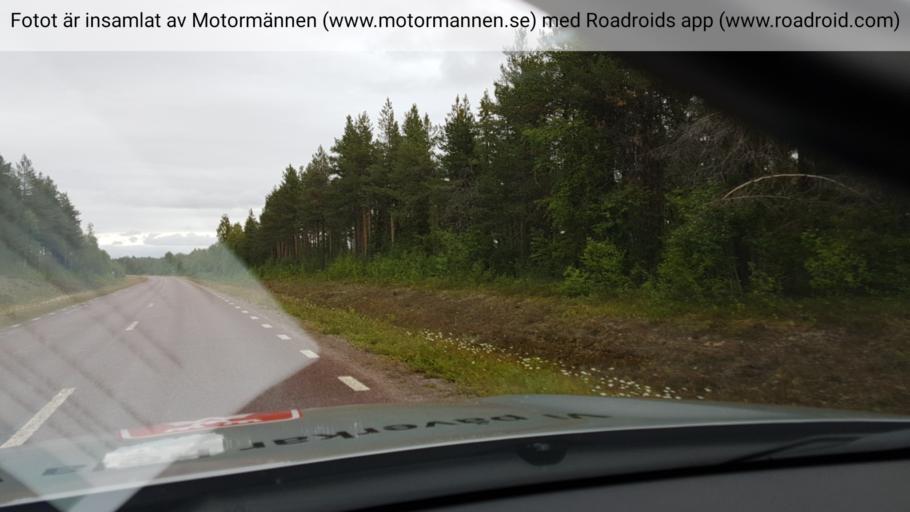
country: SE
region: Norrbotten
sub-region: Pajala Kommun
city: Pajala
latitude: 67.1464
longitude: 22.6227
